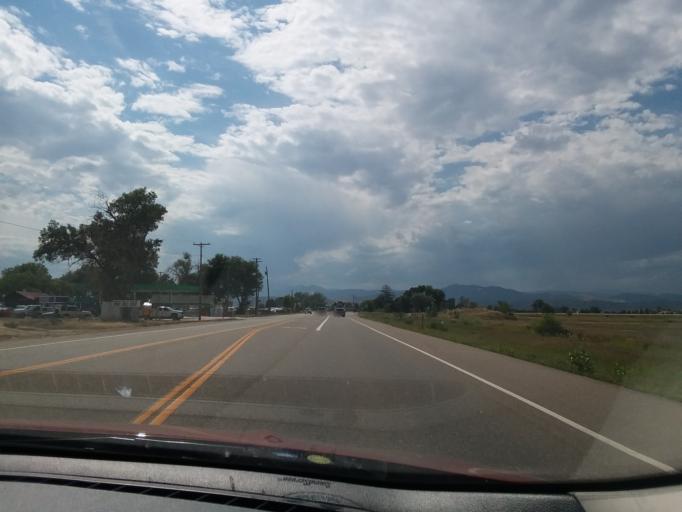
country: US
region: Colorado
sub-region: Larimer County
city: Berthoud
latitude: 40.3052
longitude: -105.1011
